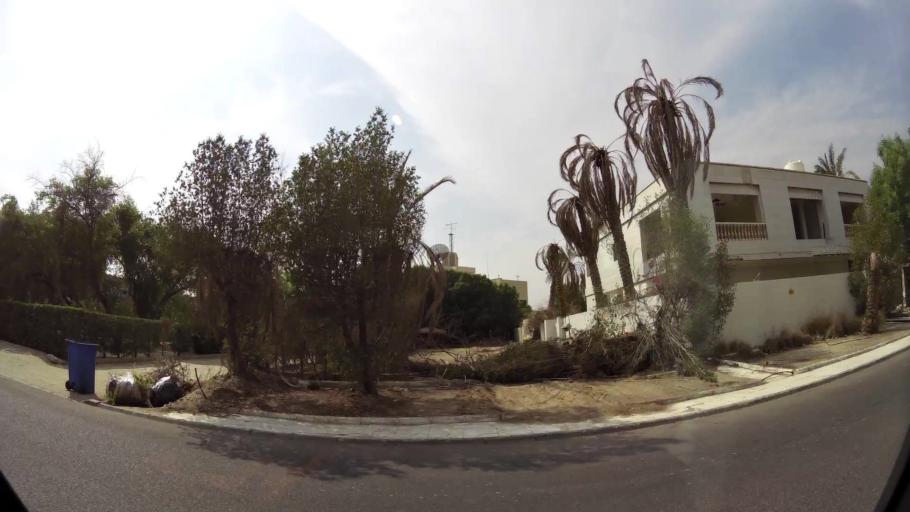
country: KW
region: Al Asimah
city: Ad Dasmah
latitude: 29.3558
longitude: 47.9878
